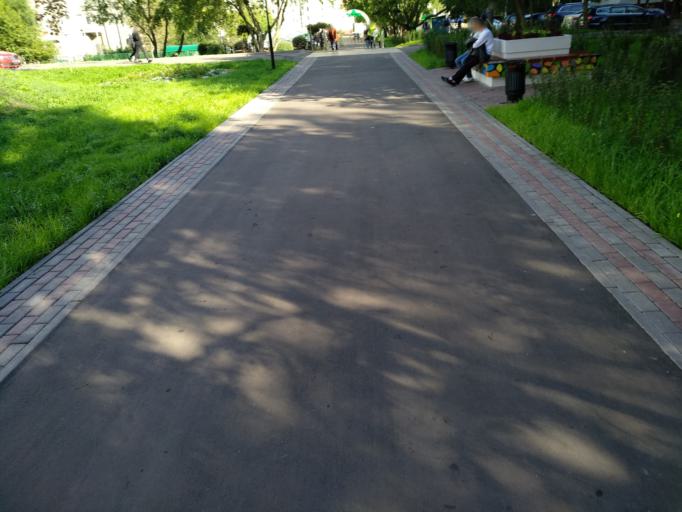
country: RU
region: Moscow
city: Yasenevo
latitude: 55.6394
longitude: 37.5303
